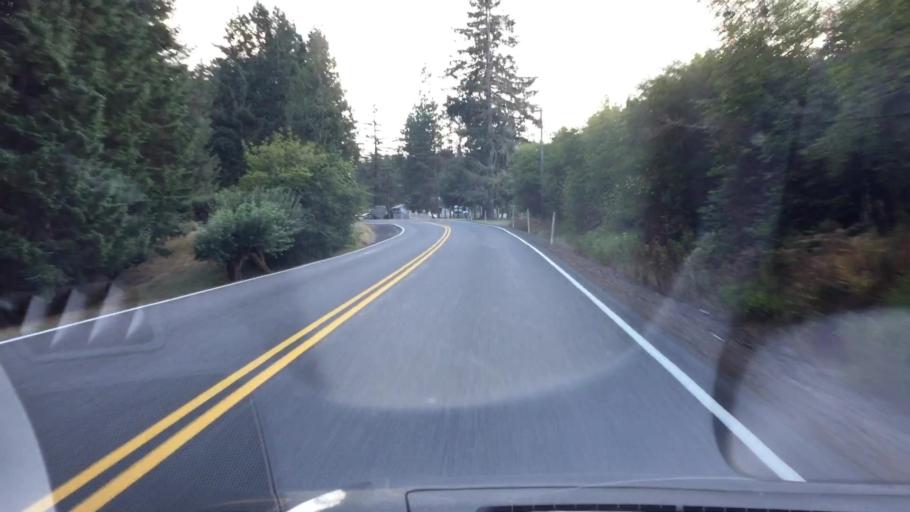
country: US
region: Washington
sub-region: Lewis County
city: Napavine
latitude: 46.5007
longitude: -122.7620
